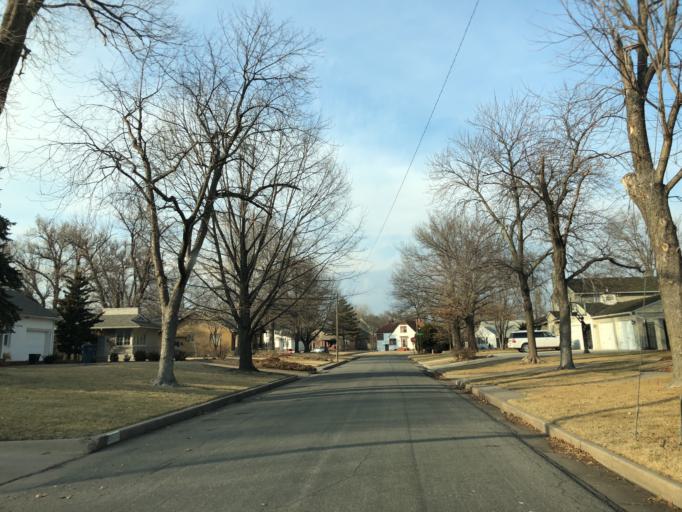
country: US
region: Kansas
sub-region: Reno County
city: Hutchinson
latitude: 38.0757
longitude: -97.9374
